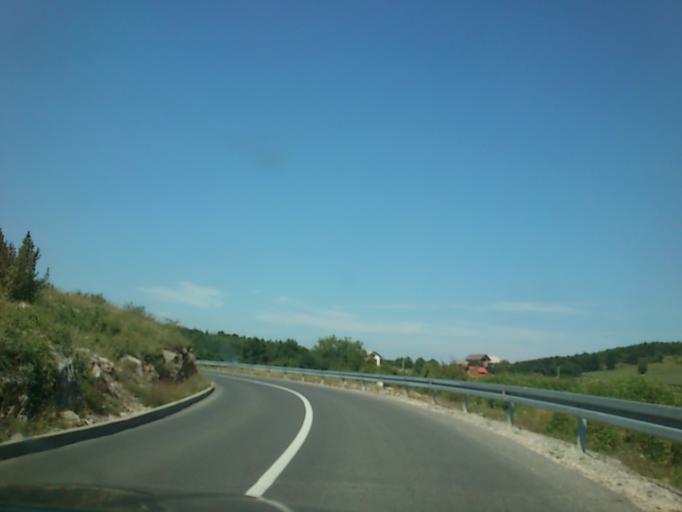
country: HR
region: Licko-Senjska
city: Otocac
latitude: 44.8541
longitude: 15.1552
